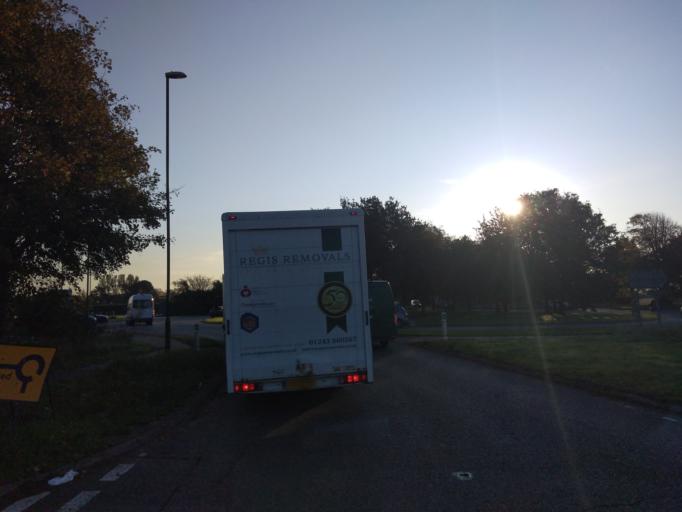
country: GB
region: England
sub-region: West Sussex
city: Rustington
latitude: 50.8184
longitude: -0.4698
